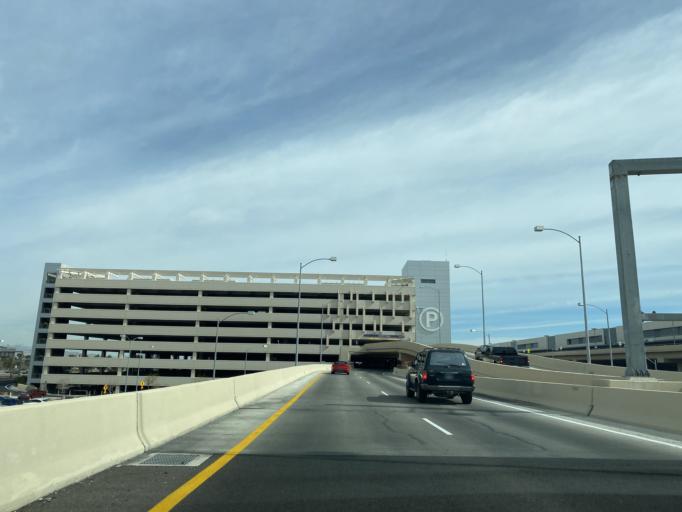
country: US
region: Nevada
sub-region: Clark County
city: Paradise
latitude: 36.0875
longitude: -115.1403
